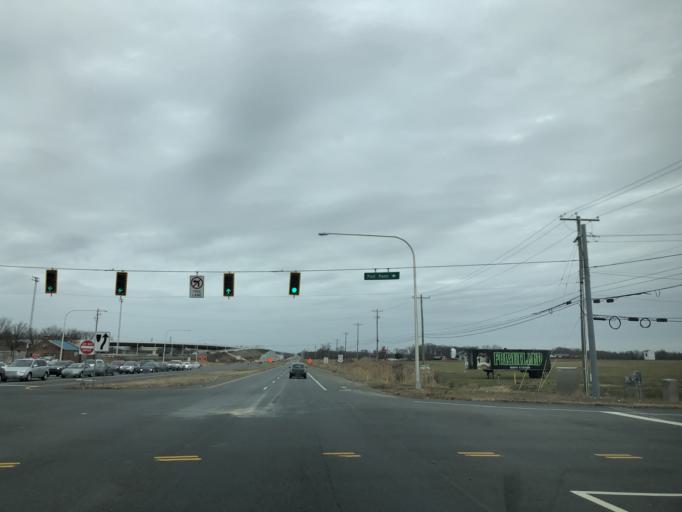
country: US
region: Delaware
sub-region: New Castle County
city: Delaware City
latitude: 39.5245
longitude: -75.6489
